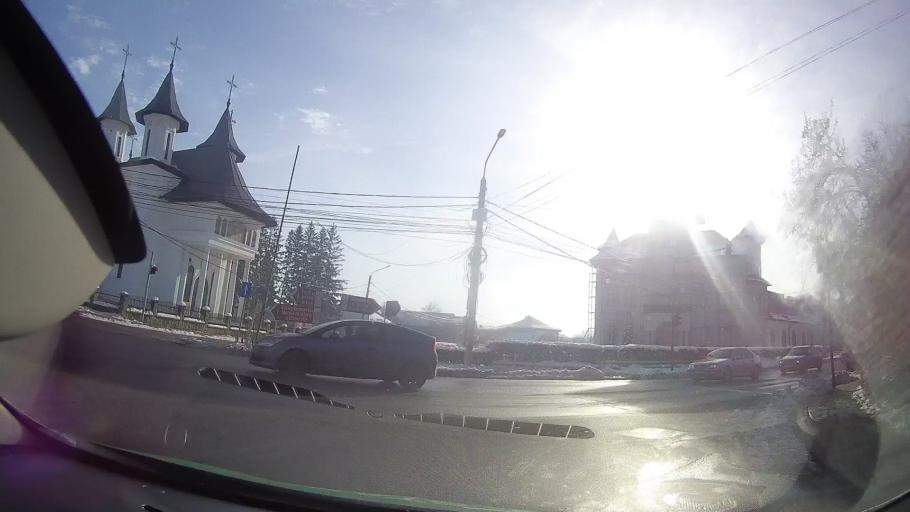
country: RO
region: Neamt
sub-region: Oras Targu Neamt
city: Humulesti
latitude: 47.1988
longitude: 26.3521
